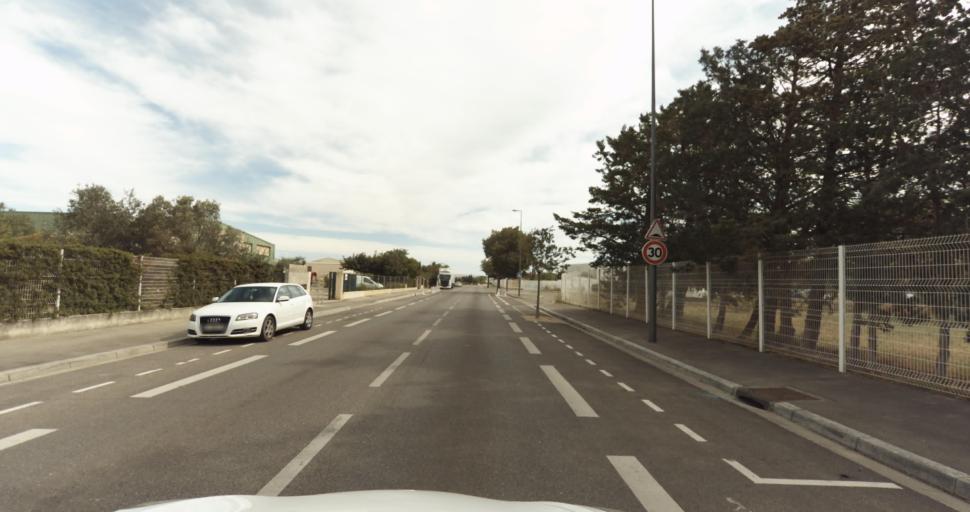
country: FR
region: Provence-Alpes-Cote d'Azur
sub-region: Departement des Bouches-du-Rhone
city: Miramas
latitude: 43.5978
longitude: 4.9999
